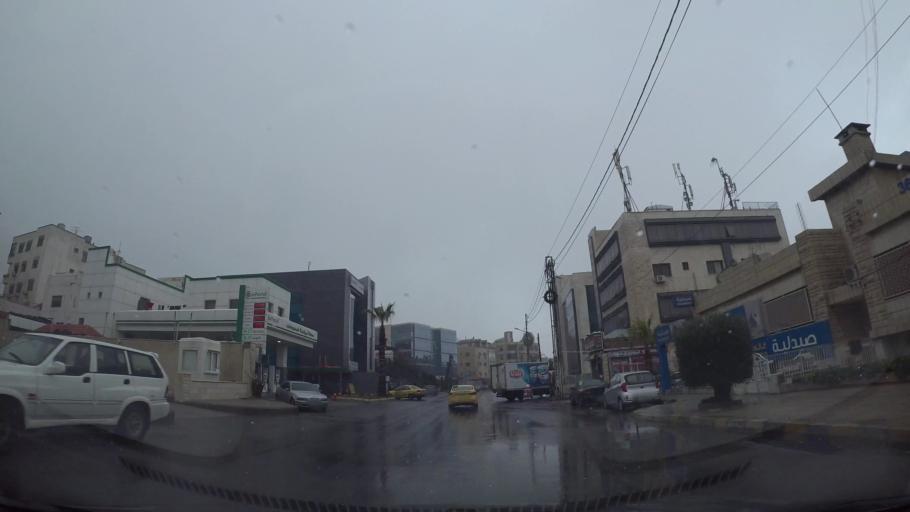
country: JO
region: Amman
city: Al Jubayhah
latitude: 31.9675
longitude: 35.8775
